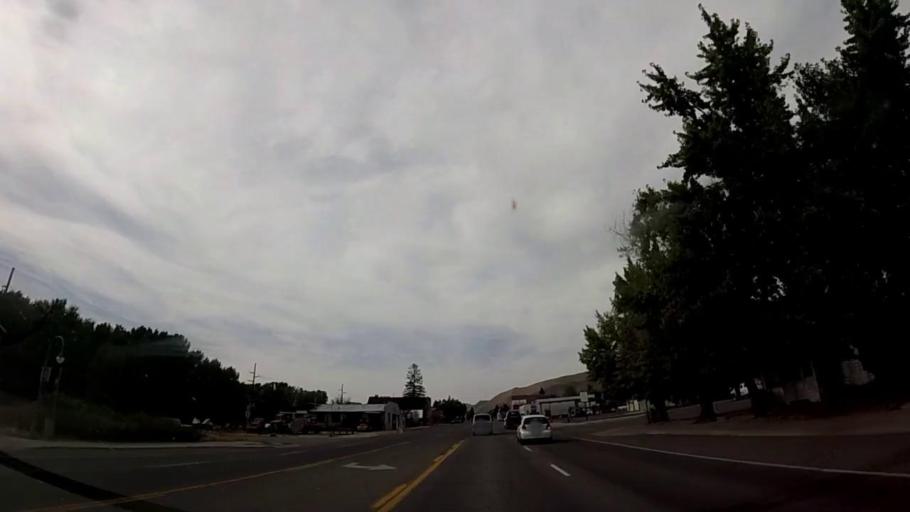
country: US
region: Idaho
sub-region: Blaine County
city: Bellevue
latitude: 43.4624
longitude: -114.2599
